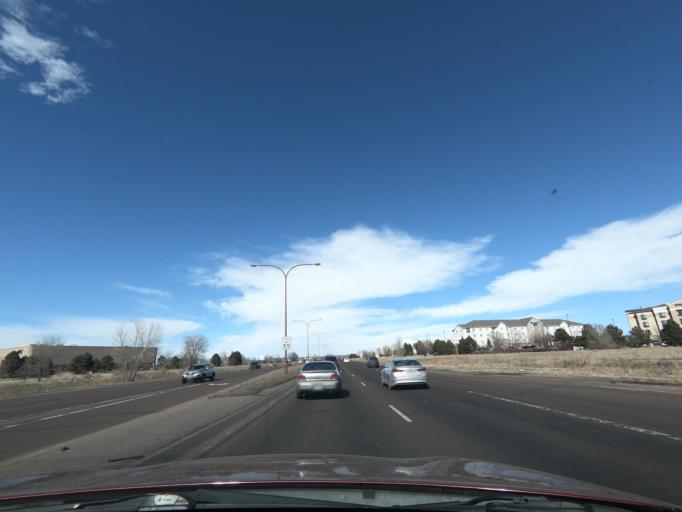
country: US
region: Colorado
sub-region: El Paso County
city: Stratmoor
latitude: 38.8070
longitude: -104.7302
